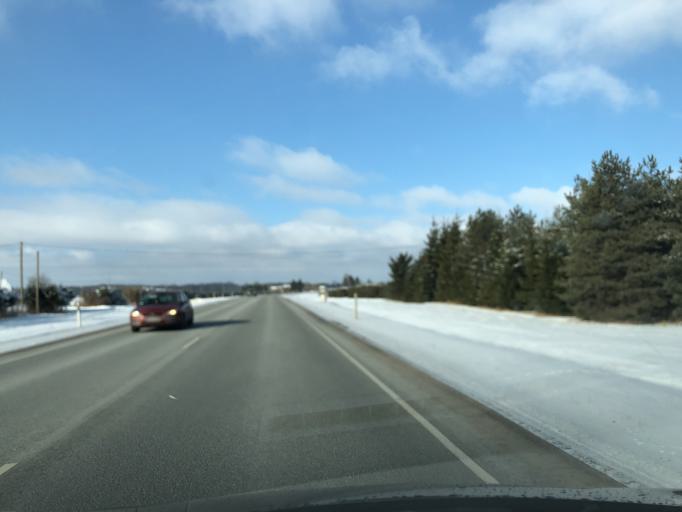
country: EE
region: Jaervamaa
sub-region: Paide linn
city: Paide
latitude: 58.8482
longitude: 25.7321
